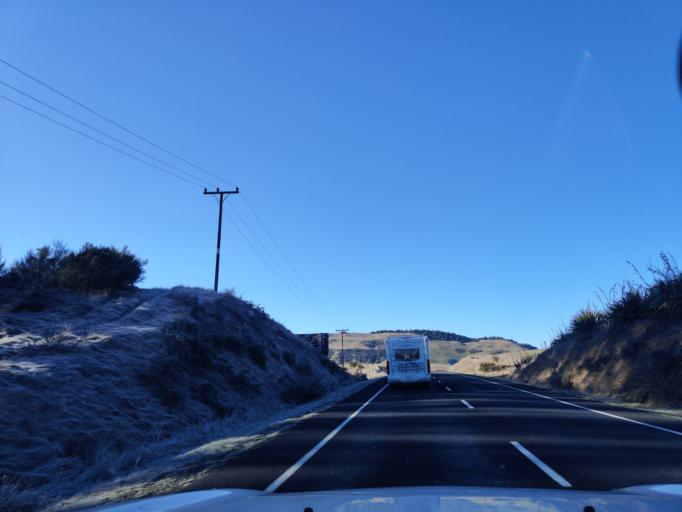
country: NZ
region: Manawatu-Wanganui
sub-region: Ruapehu District
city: Waiouru
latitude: -39.5109
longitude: 175.6817
